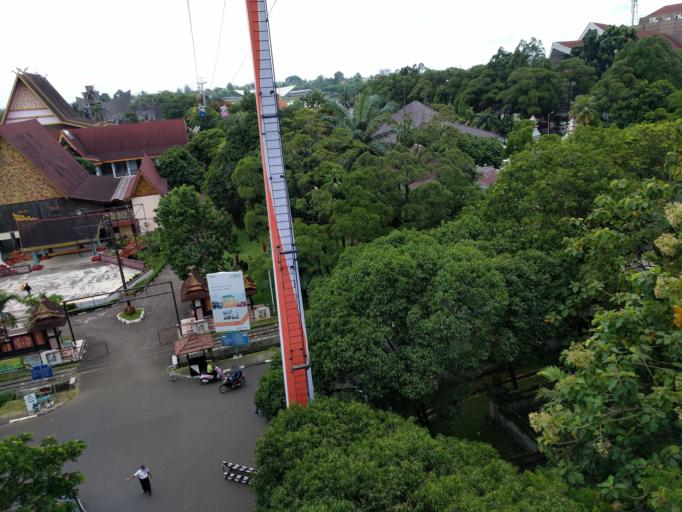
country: ID
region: Jakarta Raya
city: Jakarta
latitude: -6.3005
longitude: 106.8919
